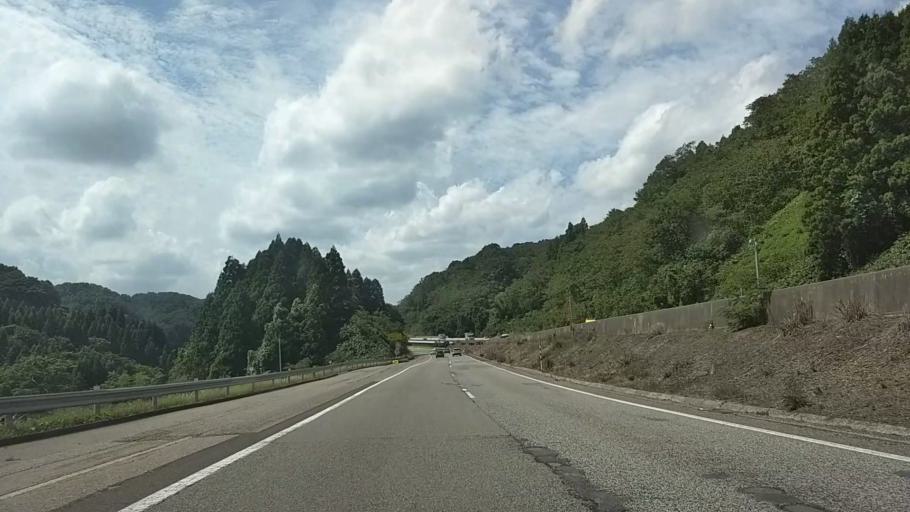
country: JP
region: Ishikawa
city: Tsubata
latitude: 36.5998
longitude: 136.7811
